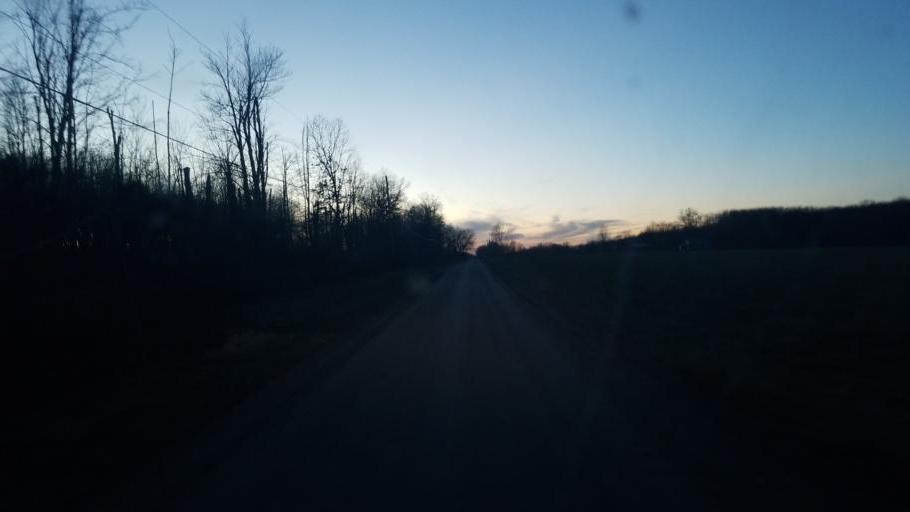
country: US
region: Ohio
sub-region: Ashtabula County
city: Andover
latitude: 41.6233
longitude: -80.6739
